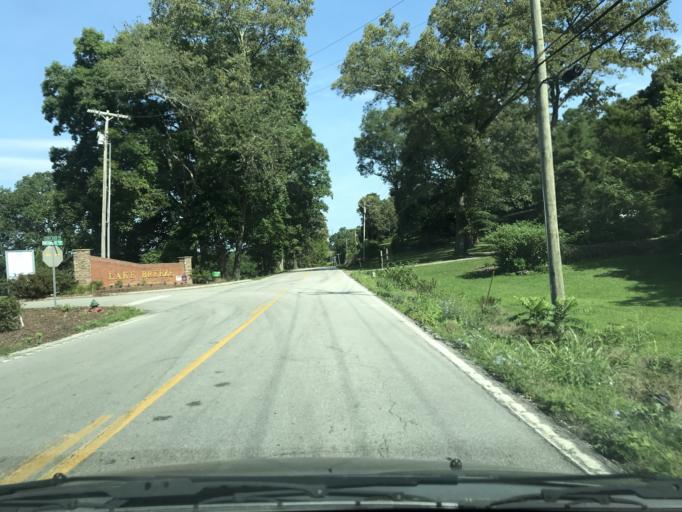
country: US
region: Tennessee
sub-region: Hamilton County
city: Lakesite
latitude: 35.2315
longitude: -85.0647
